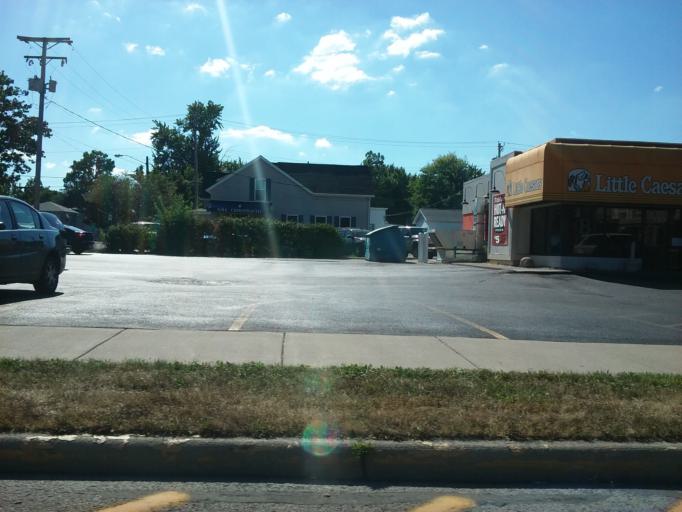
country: US
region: Ohio
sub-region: Hancock County
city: Findlay
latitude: 41.0333
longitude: -83.6503
